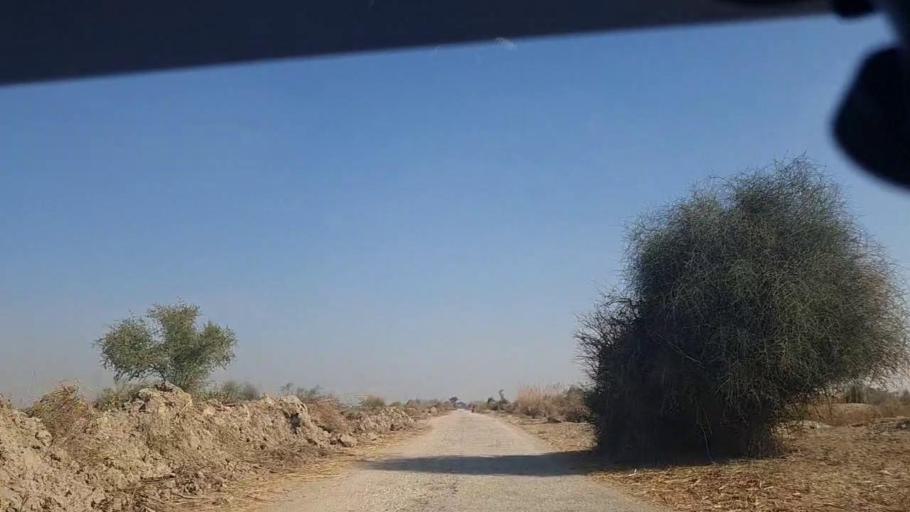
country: PK
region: Sindh
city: Khanpur
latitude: 27.5644
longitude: 69.3086
